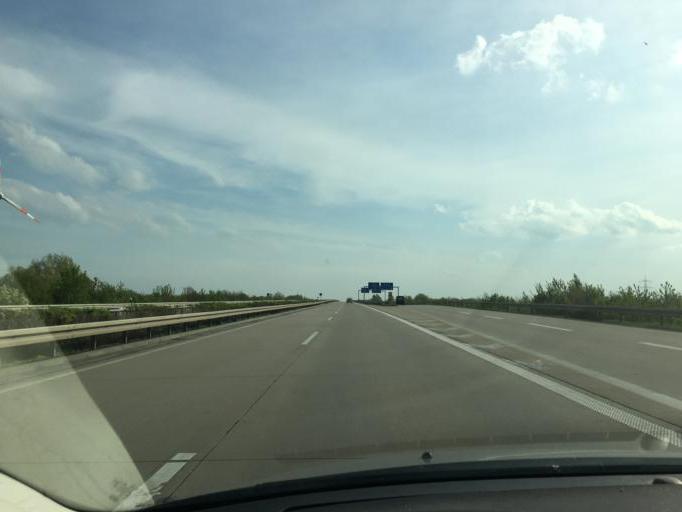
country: DE
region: Saxony-Anhalt
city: Dahlenwarsleben
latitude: 52.1760
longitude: 11.5462
